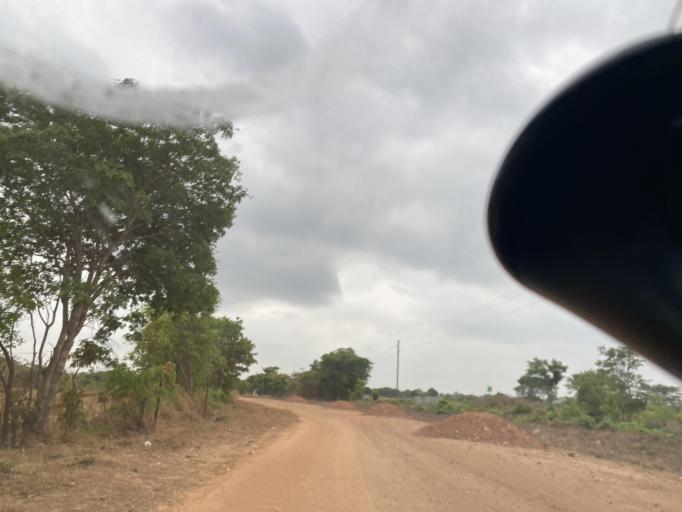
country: ZM
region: Lusaka
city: Chongwe
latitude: -15.2623
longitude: 28.7321
